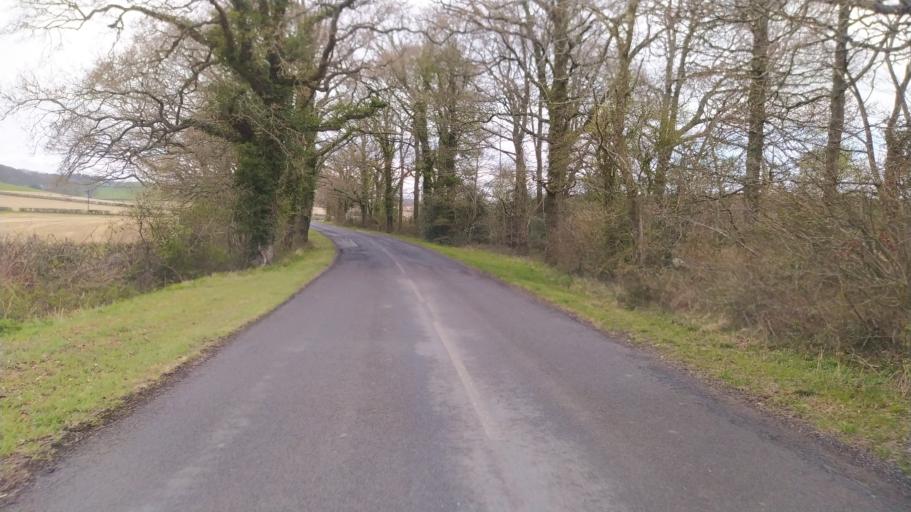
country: GB
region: England
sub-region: West Sussex
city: Petworth
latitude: 51.0117
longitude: -0.6071
